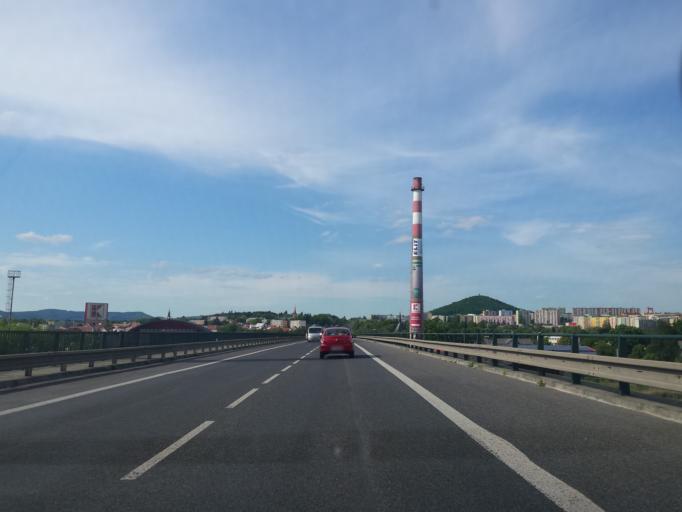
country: CZ
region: Liberecky
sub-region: Okres Ceska Lipa
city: Ceska Lipa
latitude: 50.6784
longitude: 14.5418
